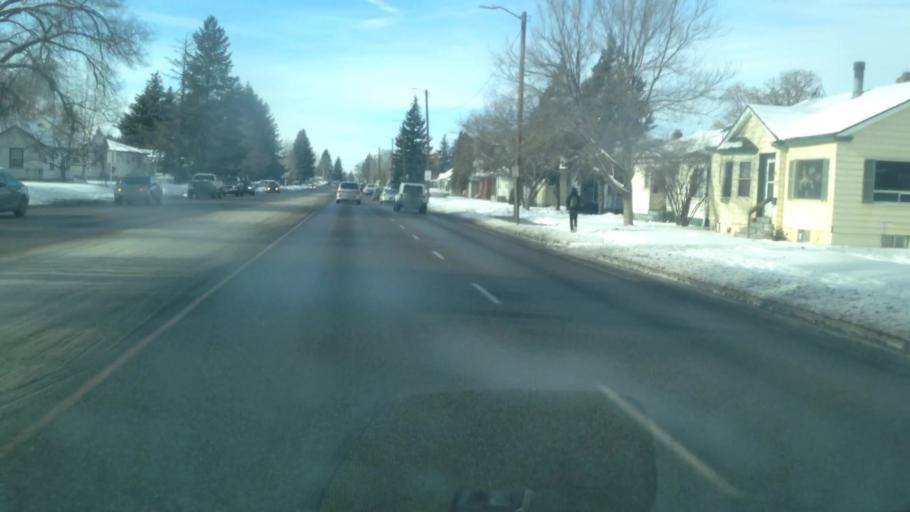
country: US
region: Idaho
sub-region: Bonneville County
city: Idaho Falls
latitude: 43.4826
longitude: -112.0263
